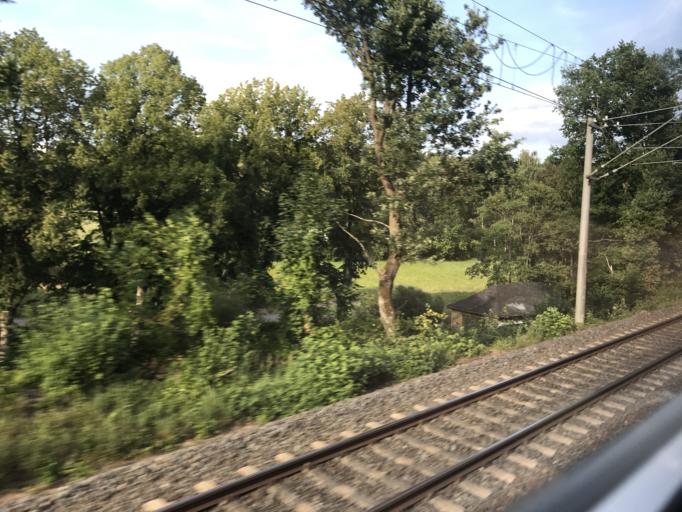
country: DE
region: Hesse
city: Bad Camberg
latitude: 50.3322
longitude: 8.2339
